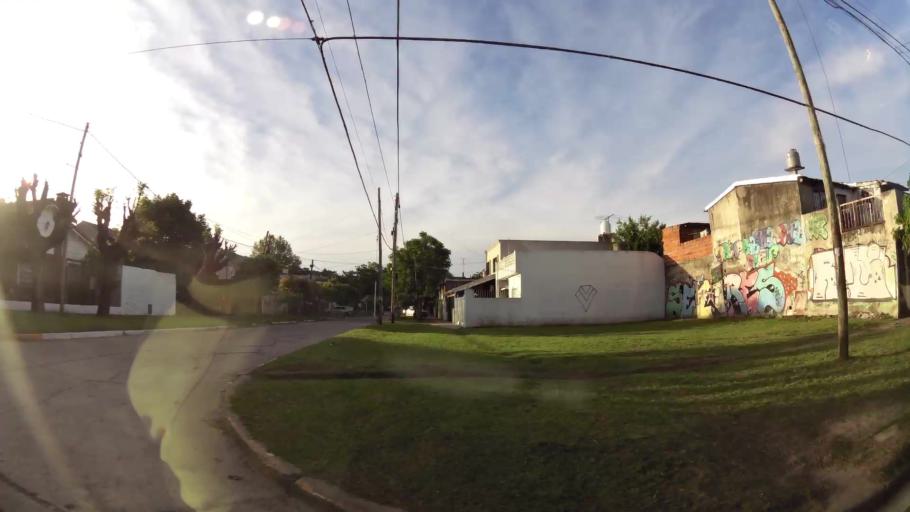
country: AR
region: Buenos Aires
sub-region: Partido de Almirante Brown
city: Adrogue
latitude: -34.7940
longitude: -58.3505
